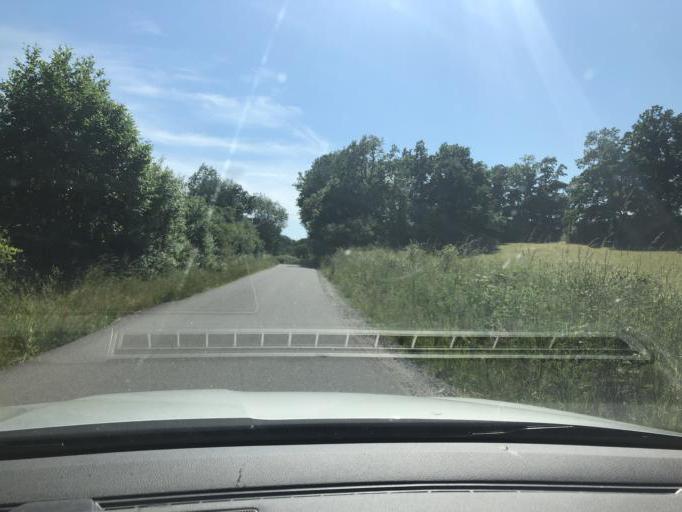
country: SE
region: Blekinge
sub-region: Karlshamns Kommun
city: Karlshamn
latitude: 56.1690
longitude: 14.8098
